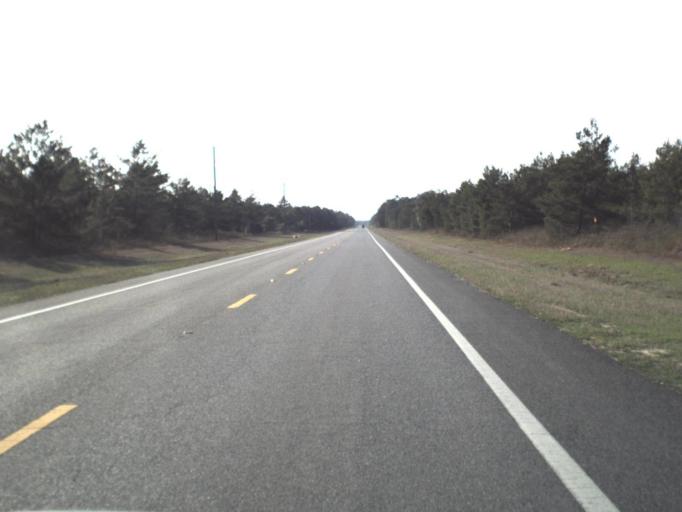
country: US
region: Florida
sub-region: Bay County
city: Lynn Haven
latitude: 30.4248
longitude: -85.6603
